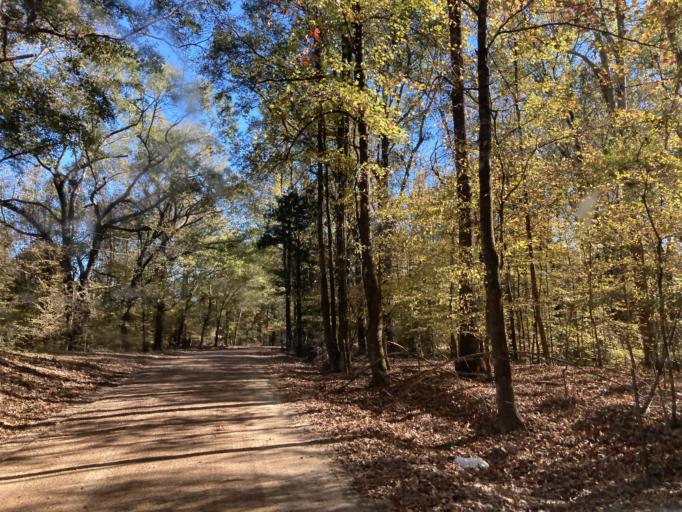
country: US
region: Mississippi
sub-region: Yazoo County
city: Yazoo City
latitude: 32.7574
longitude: -90.3888
